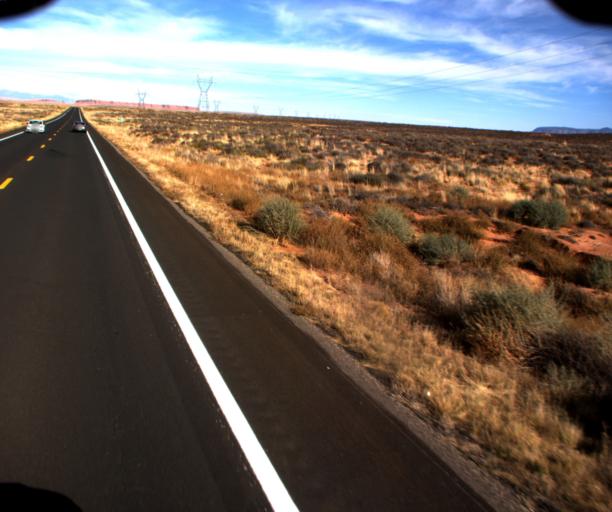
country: US
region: Arizona
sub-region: Apache County
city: Lukachukai
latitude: 36.9586
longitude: -109.4954
